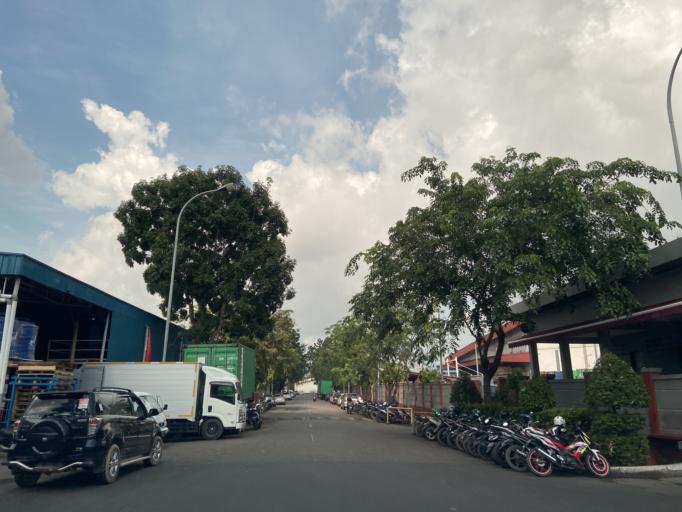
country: SG
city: Singapore
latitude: 1.1102
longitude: 104.0715
